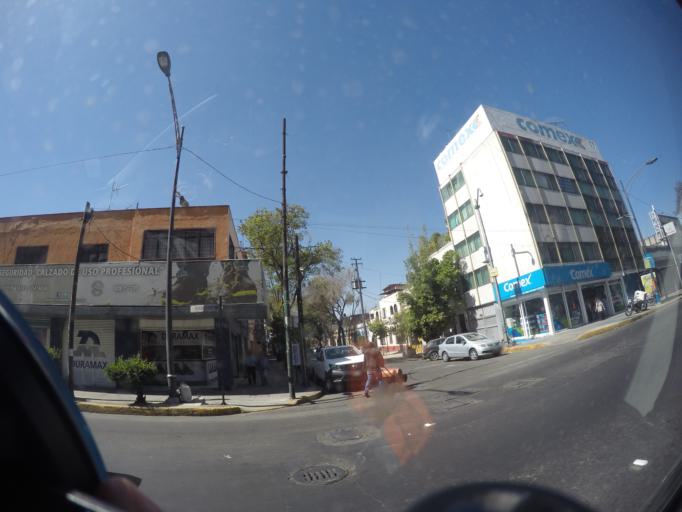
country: MX
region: Mexico City
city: Cuauhtemoc
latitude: 19.4501
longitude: -99.1526
